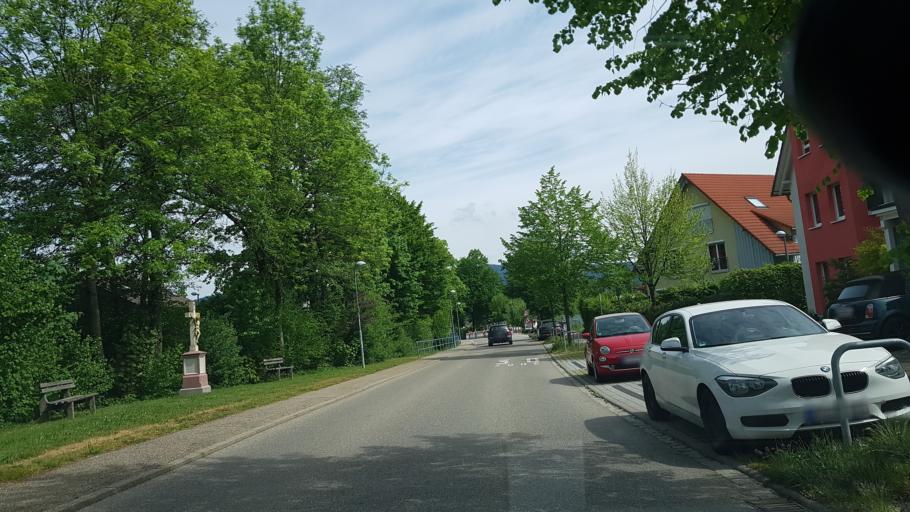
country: DE
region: Baden-Wuerttemberg
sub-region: Freiburg Region
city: Kirchzarten
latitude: 47.9679
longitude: 7.9099
